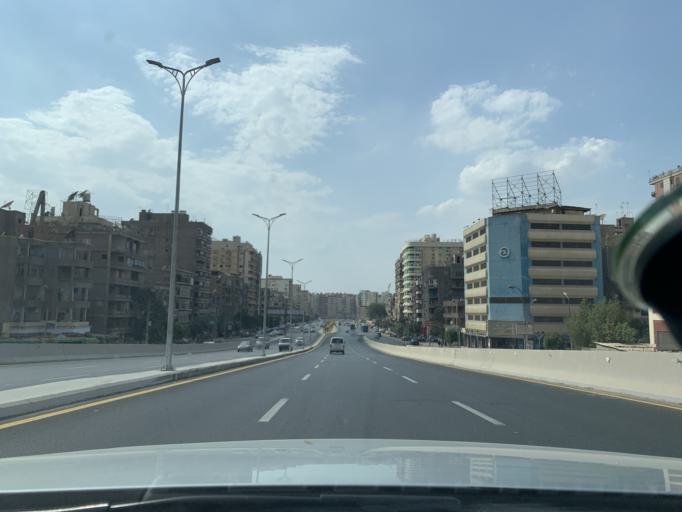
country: EG
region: Muhafazat al Qalyubiyah
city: Al Khankah
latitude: 30.1122
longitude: 31.3453
